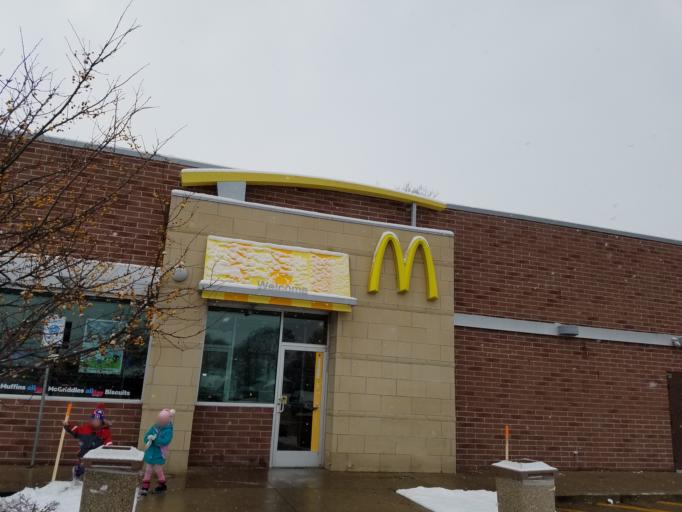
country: US
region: Michigan
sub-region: Eaton County
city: Charlotte
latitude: 42.5671
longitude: -84.8292
